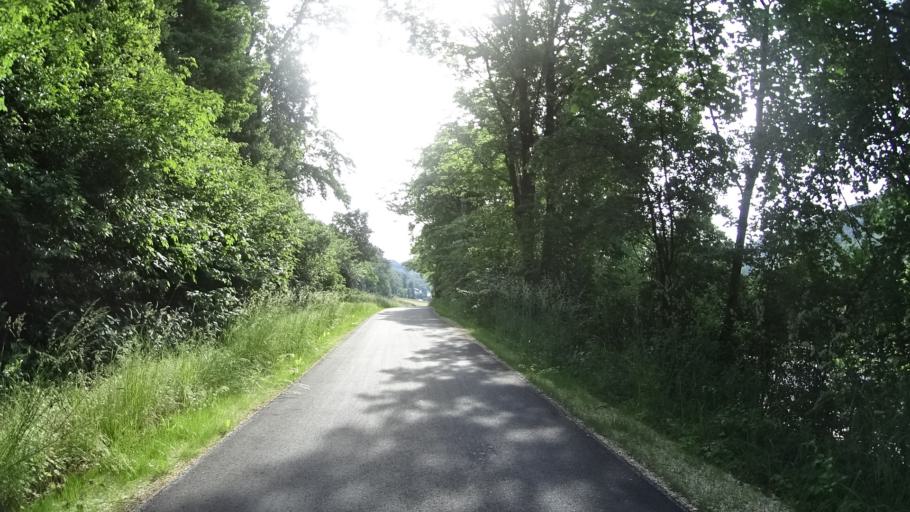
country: DE
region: Bavaria
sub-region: Lower Bavaria
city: Ihrlerstein
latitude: 48.9261
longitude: 11.8427
